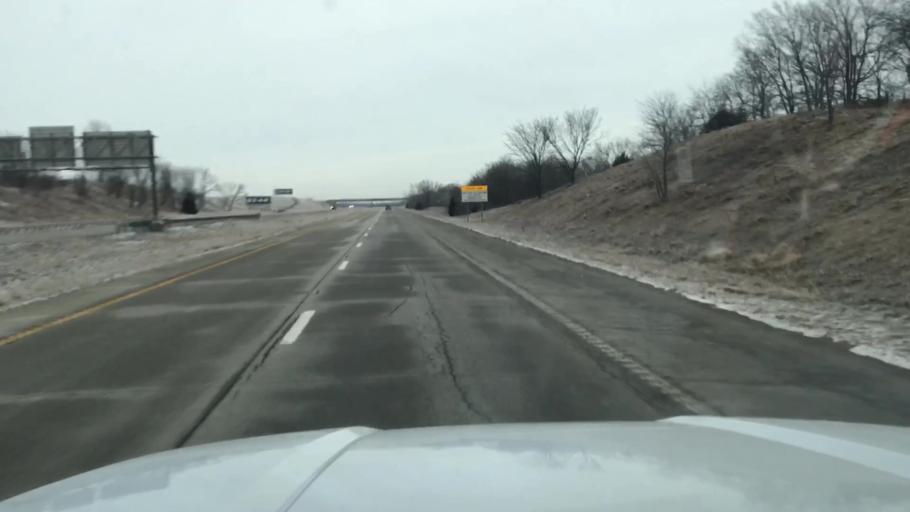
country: US
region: Missouri
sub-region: Andrew County
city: Savannah
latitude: 39.8917
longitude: -94.8570
